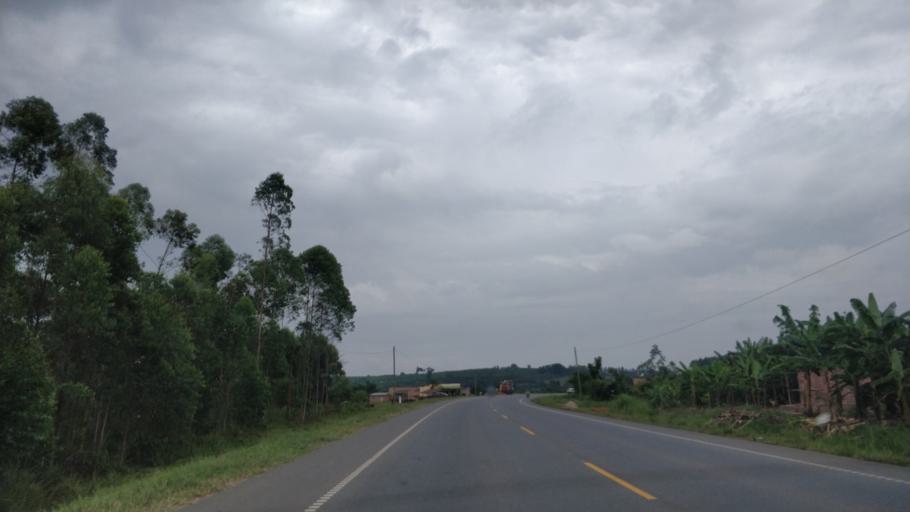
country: UG
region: Western Region
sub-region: Sheema District
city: Kibingo
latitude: -0.6511
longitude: 30.4848
